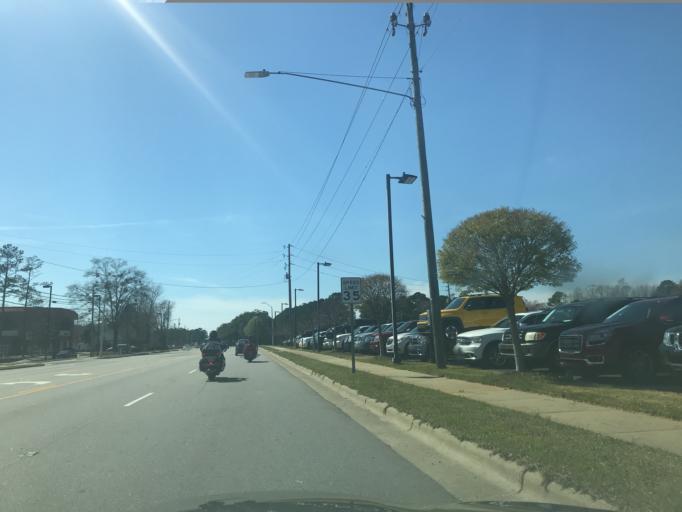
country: US
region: North Carolina
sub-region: Wake County
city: Fuquay-Varina
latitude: 35.5919
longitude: -78.7836
